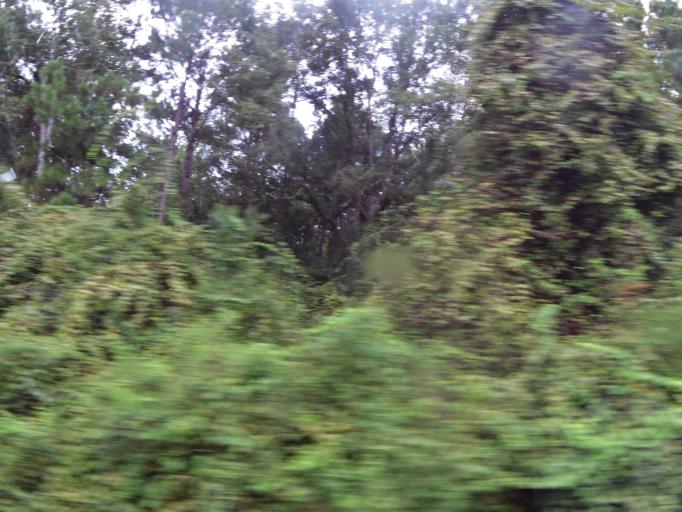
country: US
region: Florida
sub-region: Clay County
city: Lakeside
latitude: 30.1004
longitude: -81.8067
